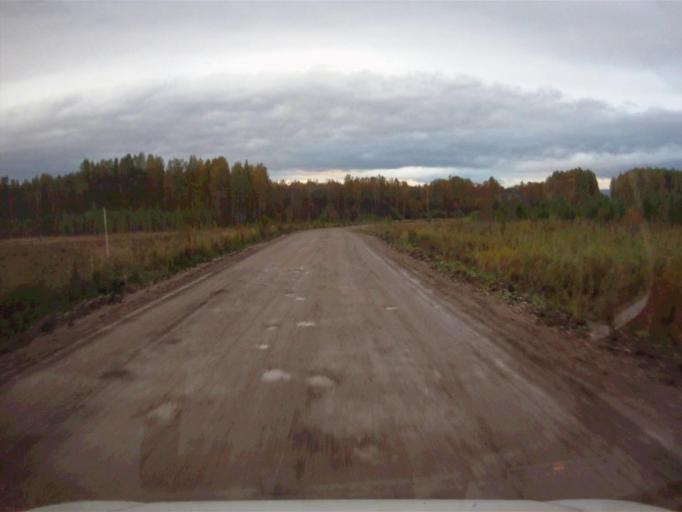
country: RU
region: Sverdlovsk
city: Mikhaylovsk
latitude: 56.1896
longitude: 59.1883
